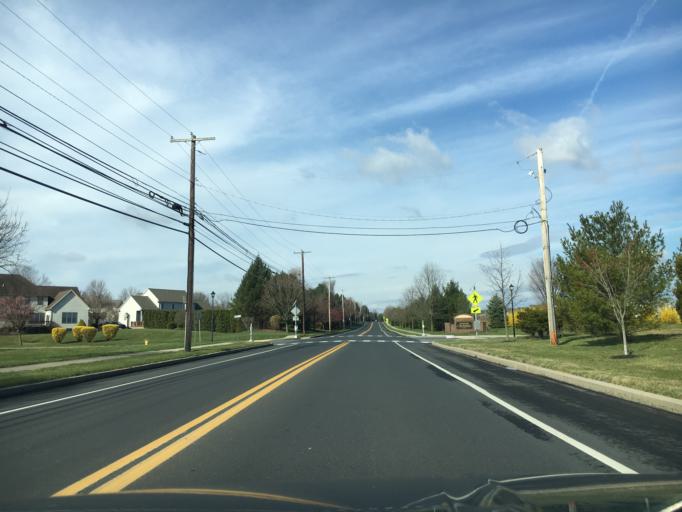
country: US
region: Pennsylvania
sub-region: Northampton County
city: Bath
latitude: 40.6815
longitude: -75.3951
